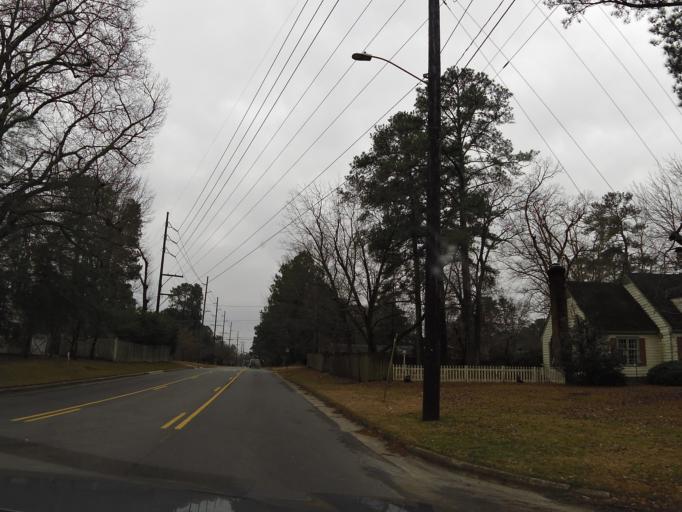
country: US
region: North Carolina
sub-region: Nash County
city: Rocky Mount
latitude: 35.9578
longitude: -77.8489
